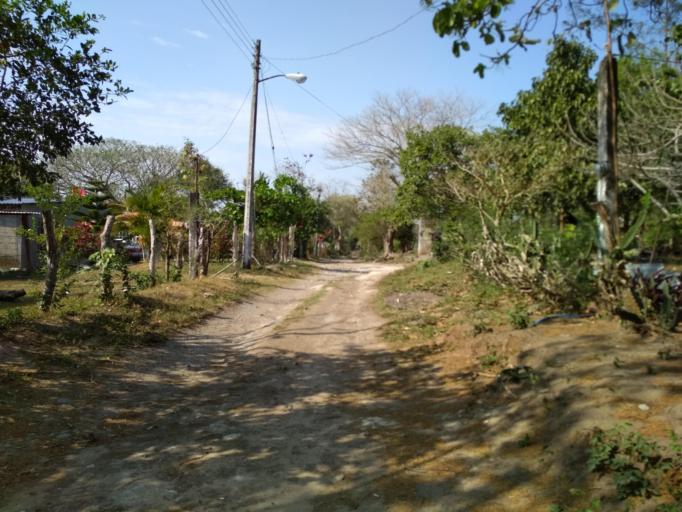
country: MX
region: Veracruz
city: Manlio Fabio Altamirano
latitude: 19.1521
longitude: -96.3087
